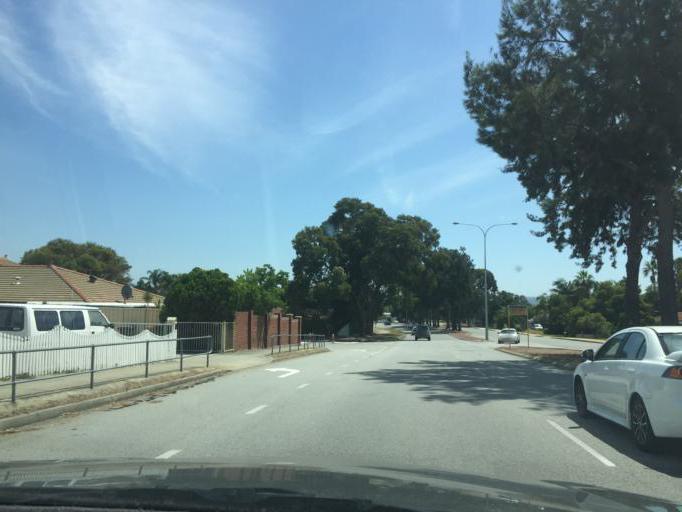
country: AU
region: Western Australia
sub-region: Gosnells
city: Thornlie
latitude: -32.0701
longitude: 115.9675
